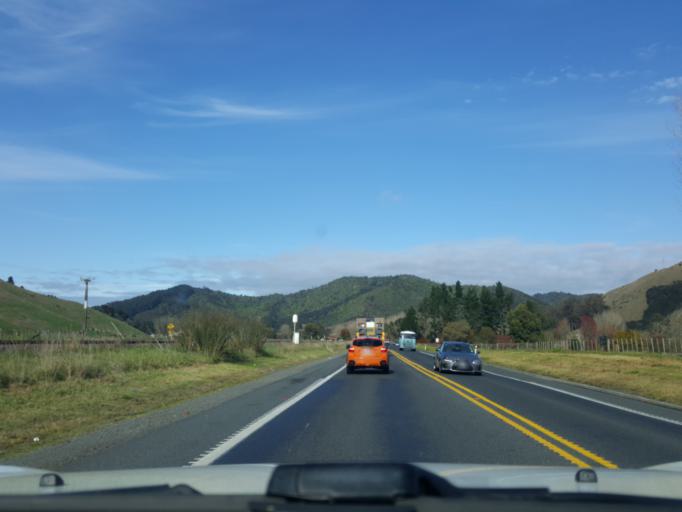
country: NZ
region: Waikato
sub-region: Waikato District
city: Ngaruawahia
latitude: -37.5875
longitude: 175.1595
